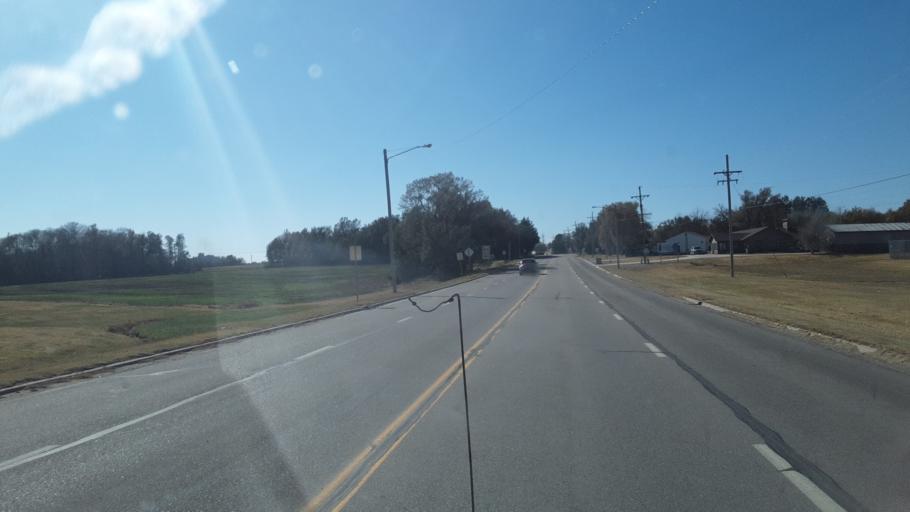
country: US
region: Kansas
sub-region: Rice County
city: Lyons
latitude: 38.3522
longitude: -98.1842
